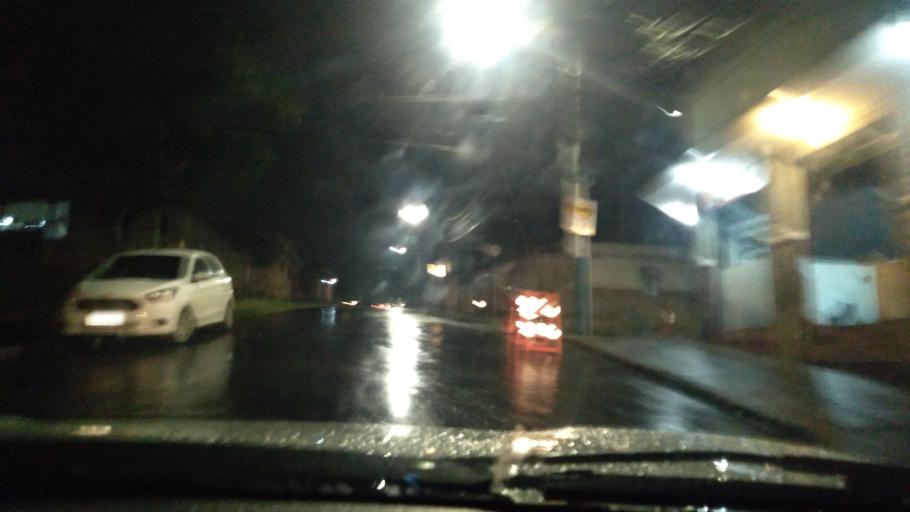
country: BR
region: Minas Gerais
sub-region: Belo Horizonte
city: Belo Horizonte
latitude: -19.8975
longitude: -43.9596
